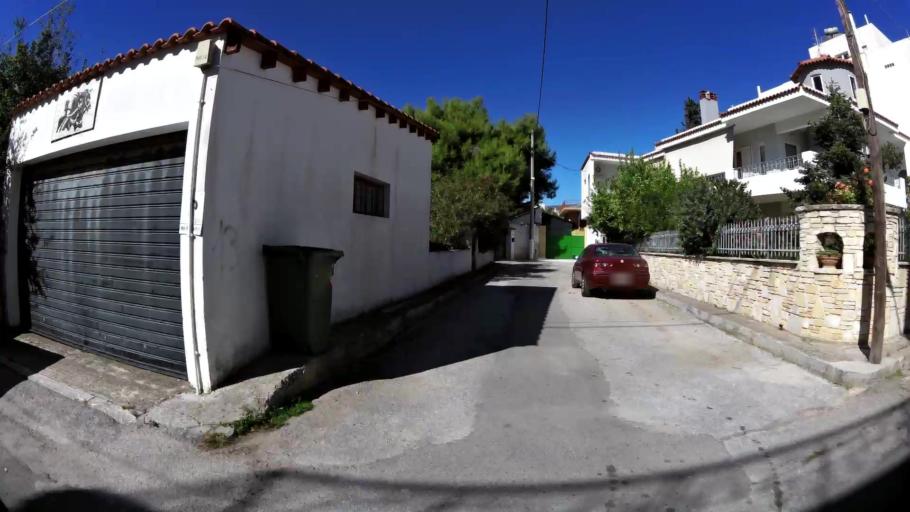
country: GR
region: Attica
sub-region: Nomarchia Anatolikis Attikis
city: Koropi
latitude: 37.8981
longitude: 23.8771
